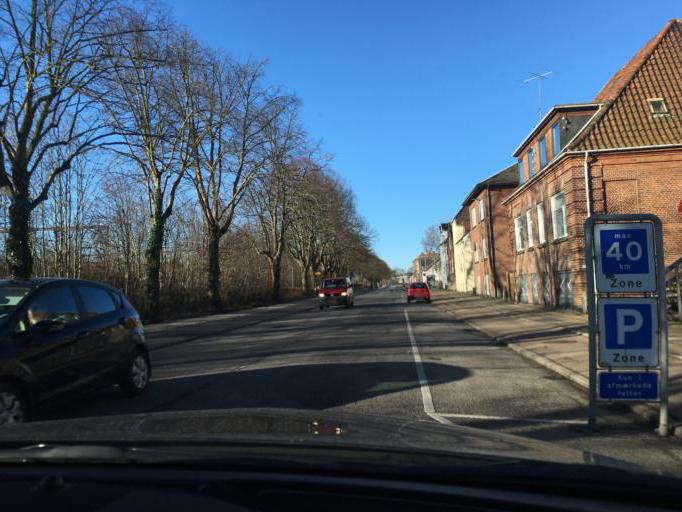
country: DK
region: South Denmark
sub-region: Kolding Kommune
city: Kolding
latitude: 55.4948
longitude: 9.4893
